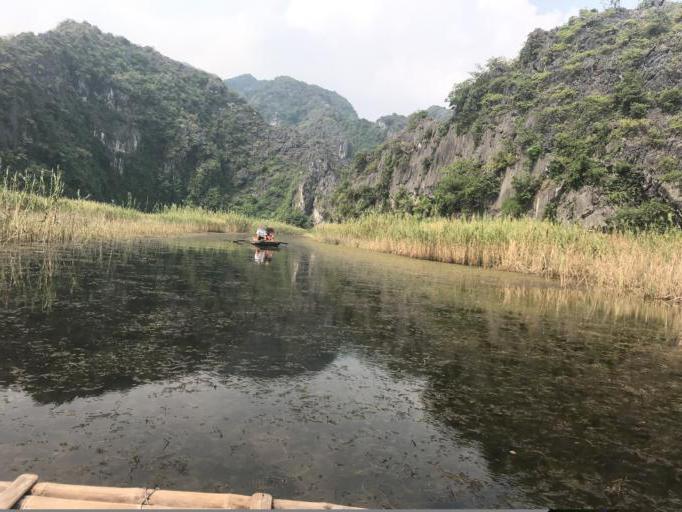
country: VN
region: Ninh Binh
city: Thi Tran Me
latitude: 20.3643
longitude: 105.8898
